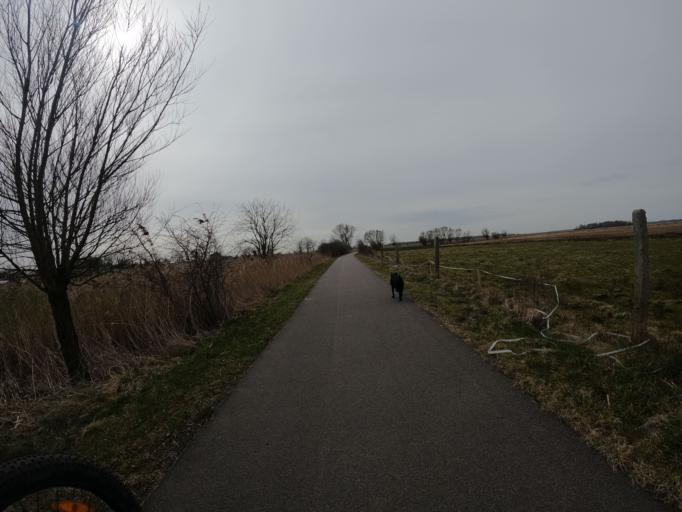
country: PL
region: West Pomeranian Voivodeship
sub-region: Powiat gryficki
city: Mrzezyno
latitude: 54.1251
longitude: 15.3139
